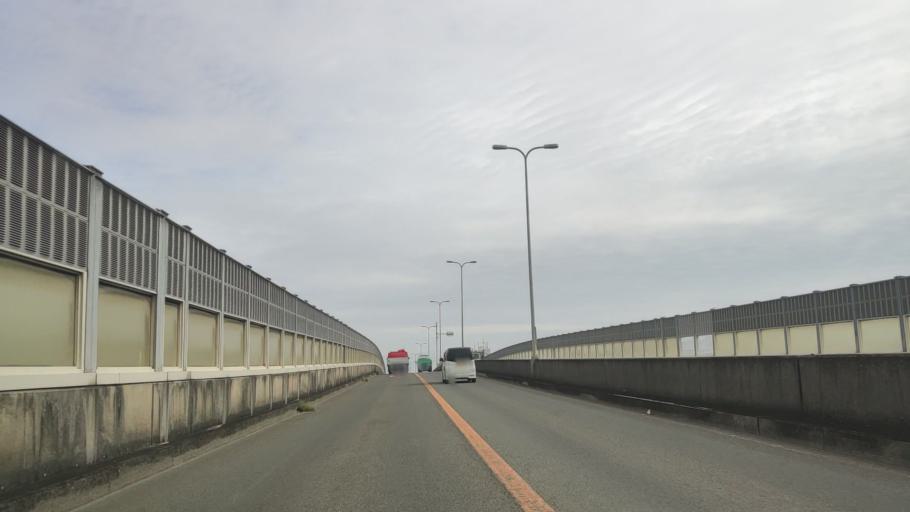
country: JP
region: Osaka
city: Kashihara
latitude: 34.5580
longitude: 135.5992
